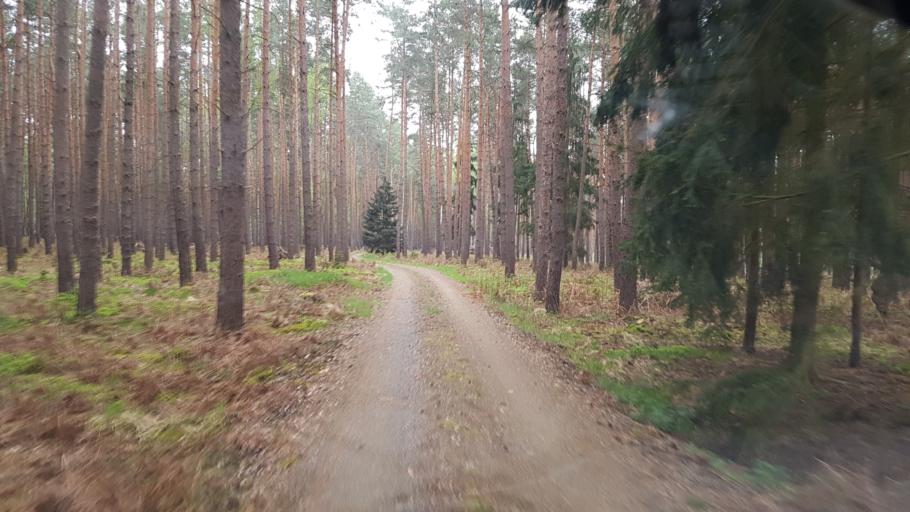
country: DE
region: Brandenburg
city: Schonewalde
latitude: 51.7193
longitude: 13.5461
